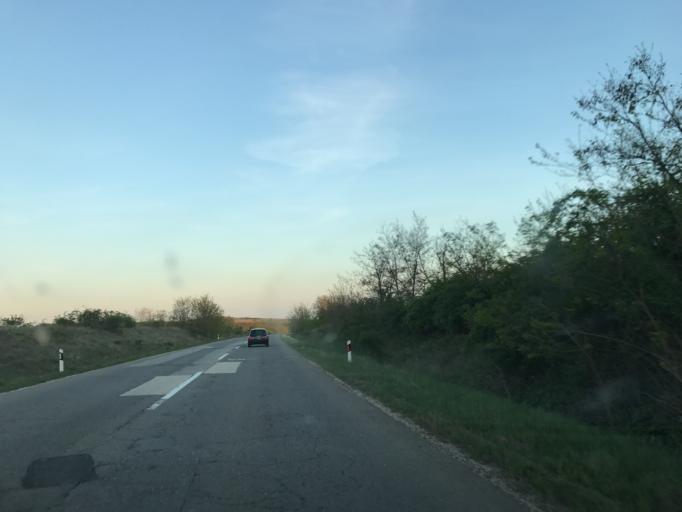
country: RO
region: Mehedinti
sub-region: Comuna Gogosu
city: Ostrovu Mare
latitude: 44.3209
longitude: 22.4917
